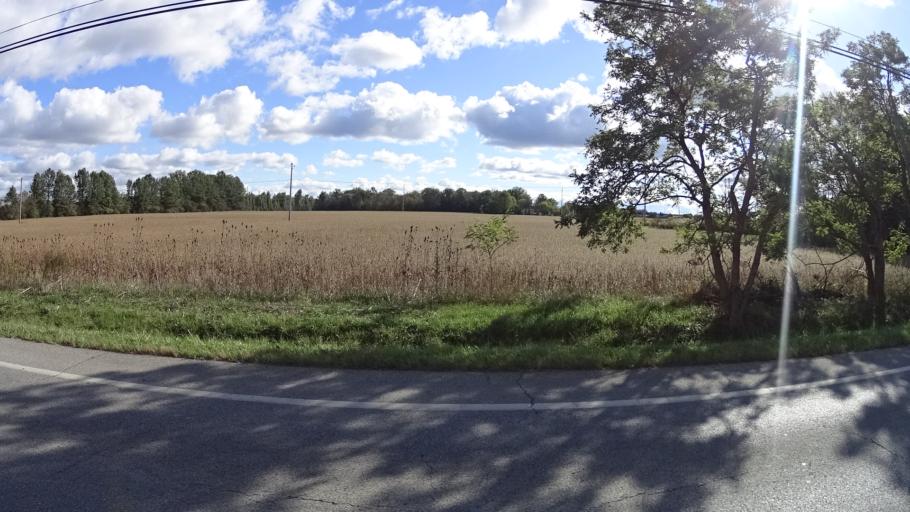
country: US
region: Ohio
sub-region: Lorain County
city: Grafton
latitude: 41.3047
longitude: -82.0701
